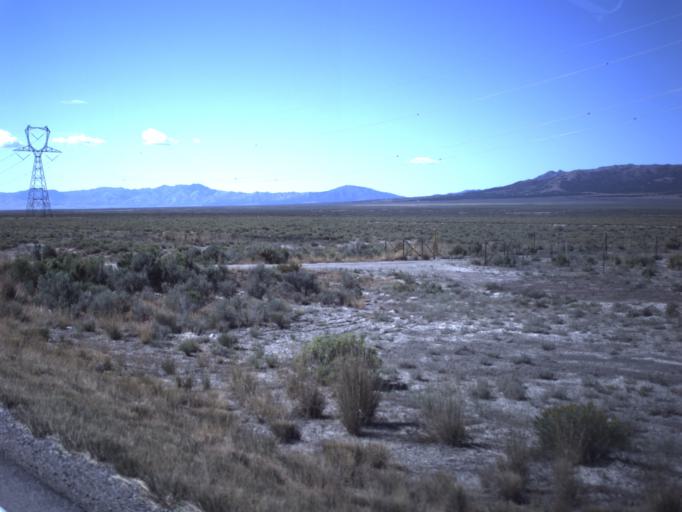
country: US
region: Utah
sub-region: Tooele County
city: Tooele
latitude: 40.2950
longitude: -112.4015
